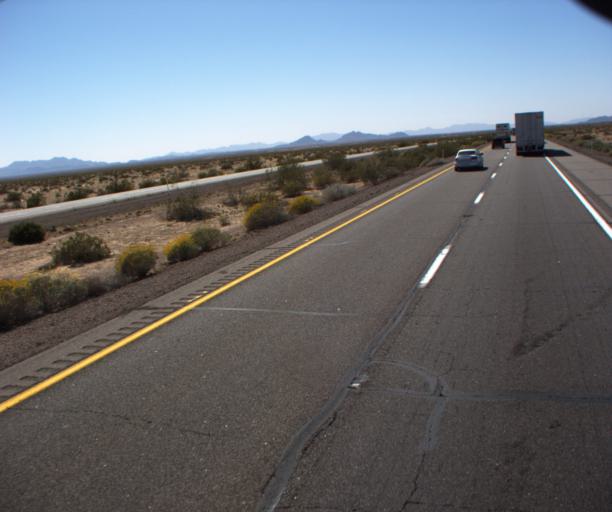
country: US
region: Arizona
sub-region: Yuma County
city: Wellton
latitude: 32.7137
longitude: -113.8218
